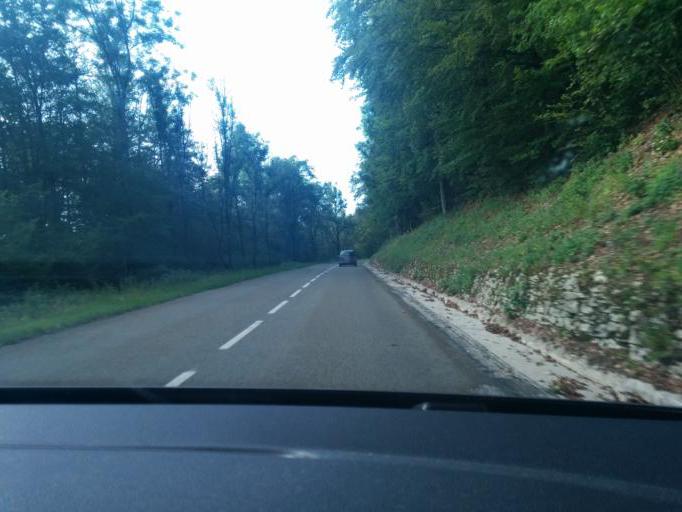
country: FR
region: Franche-Comte
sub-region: Departement du Jura
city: Saint-Lupicin
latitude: 46.4523
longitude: 5.8033
